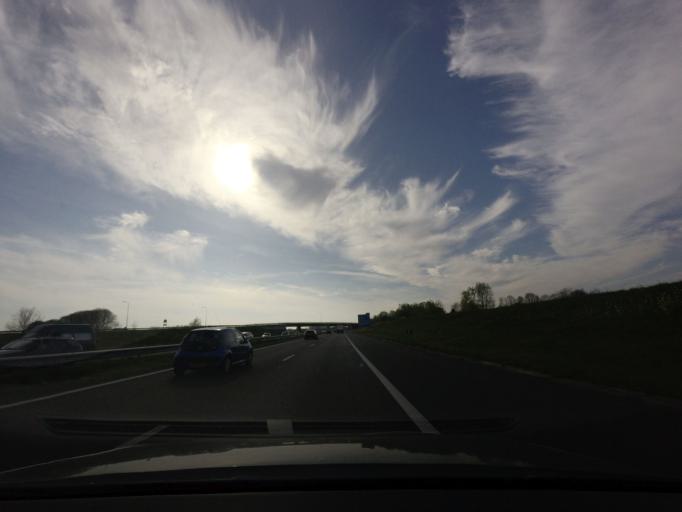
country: NL
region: North Brabant
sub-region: Gemeente Veghel
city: Veghel
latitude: 51.6326
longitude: 5.5274
